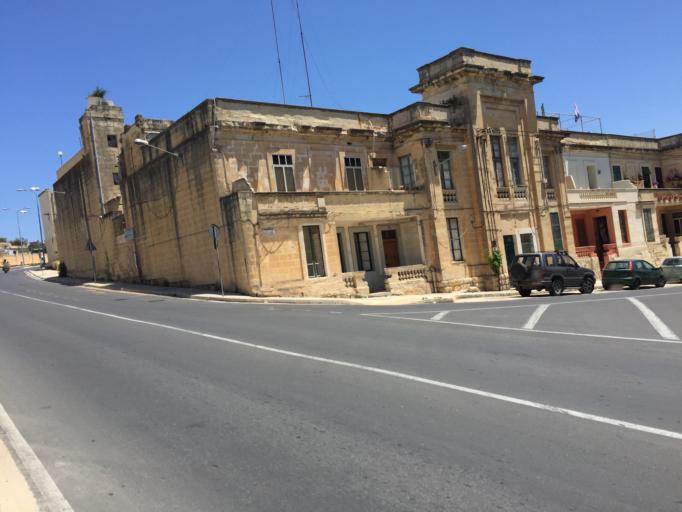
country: MT
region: Il-Marsa
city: Marsa
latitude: 35.8866
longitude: 14.4983
